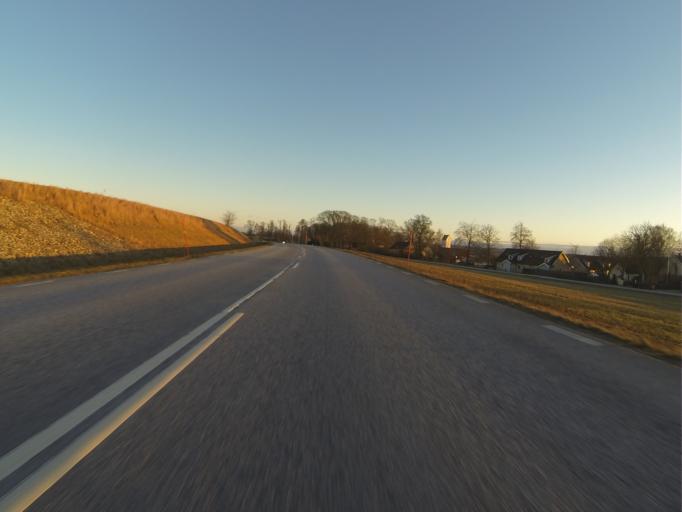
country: SE
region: Skane
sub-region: Eslovs Kommun
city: Eslov
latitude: 55.7627
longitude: 13.3255
